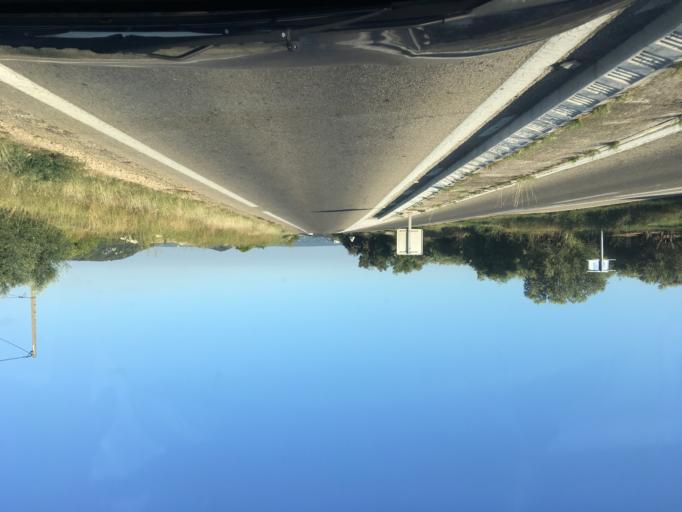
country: FR
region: Languedoc-Roussillon
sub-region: Departement du Gard
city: Ledenon
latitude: 43.9097
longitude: 4.5236
